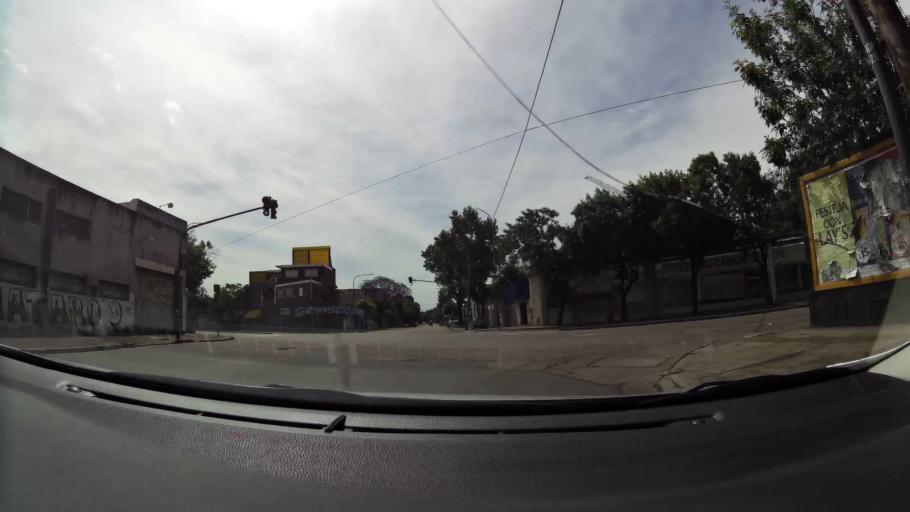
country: AR
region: Buenos Aires
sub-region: Partido de Avellaneda
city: Avellaneda
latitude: -34.6501
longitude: -58.4207
